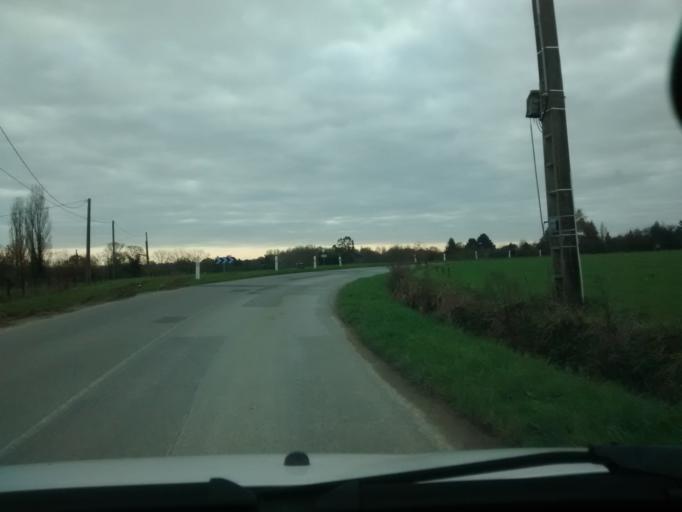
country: FR
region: Brittany
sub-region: Departement d'Ille-et-Vilaine
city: Vezin-le-Coquet
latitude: 48.0982
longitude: -1.7501
